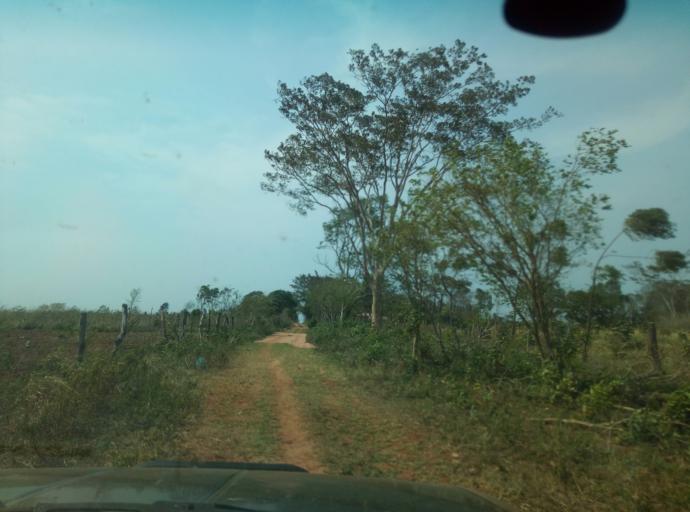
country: PY
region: Caaguazu
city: San Joaquin
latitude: -25.1440
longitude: -56.1006
